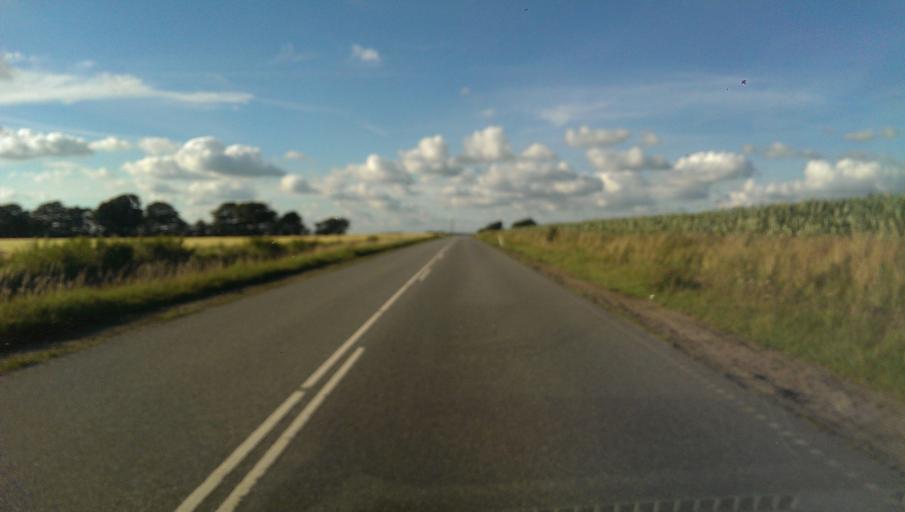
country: DK
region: South Denmark
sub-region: Esbjerg Kommune
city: Tjaereborg
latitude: 55.5095
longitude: 8.5498
